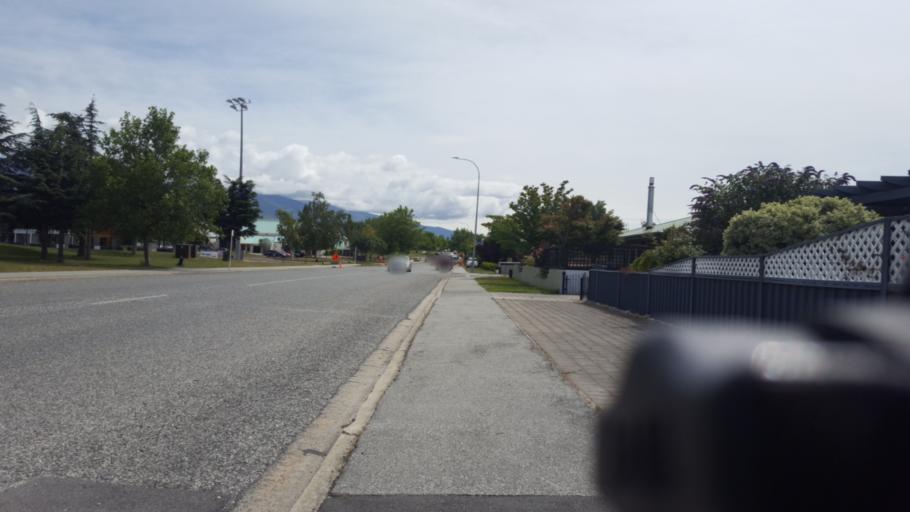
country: NZ
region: Otago
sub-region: Queenstown-Lakes District
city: Wanaka
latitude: -45.0407
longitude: 169.1976
